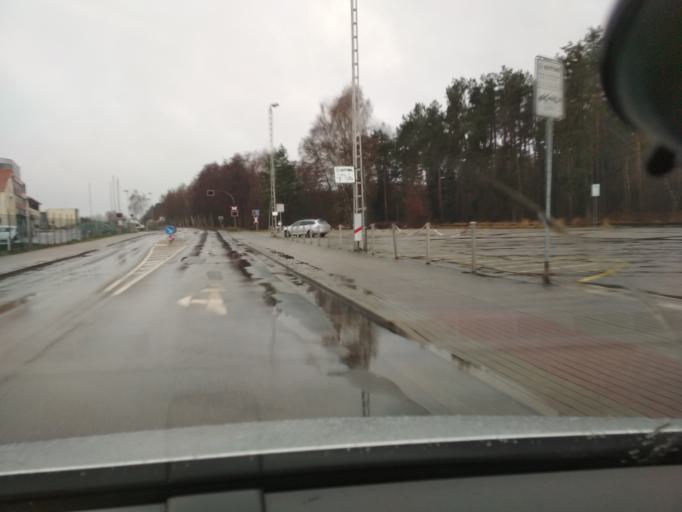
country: DE
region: Lower Saxony
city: Schoneworde
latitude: 52.6726
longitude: 10.6869
